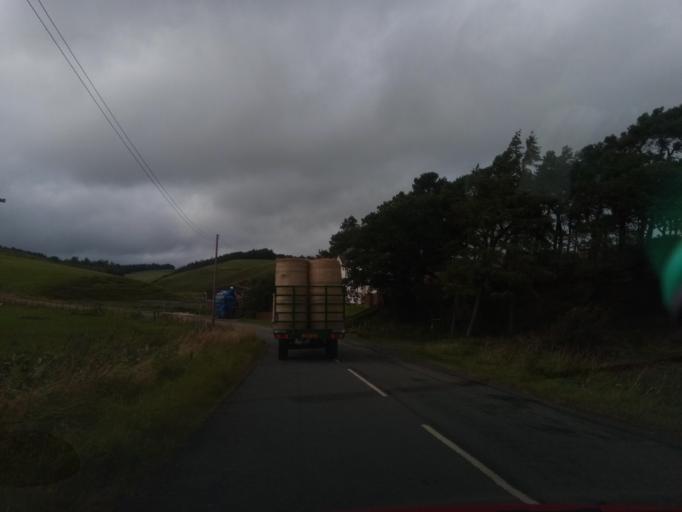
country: GB
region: Scotland
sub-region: The Scottish Borders
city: Duns
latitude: 55.8336
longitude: -2.4361
